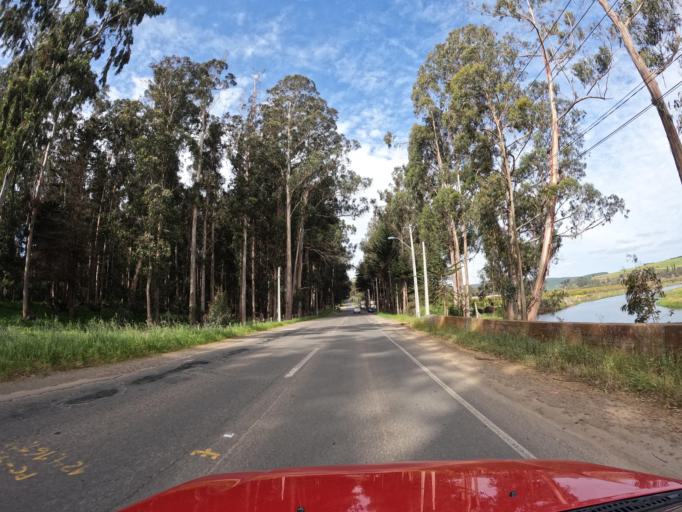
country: CL
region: O'Higgins
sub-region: Provincia de Colchagua
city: Santa Cruz
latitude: -34.3842
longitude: -71.9823
